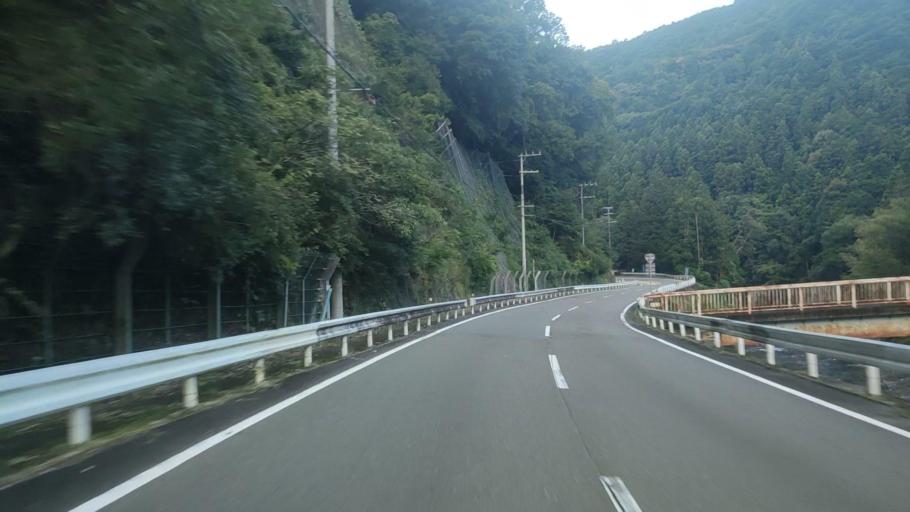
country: JP
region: Wakayama
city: Shingu
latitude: 33.8063
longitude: 135.7325
